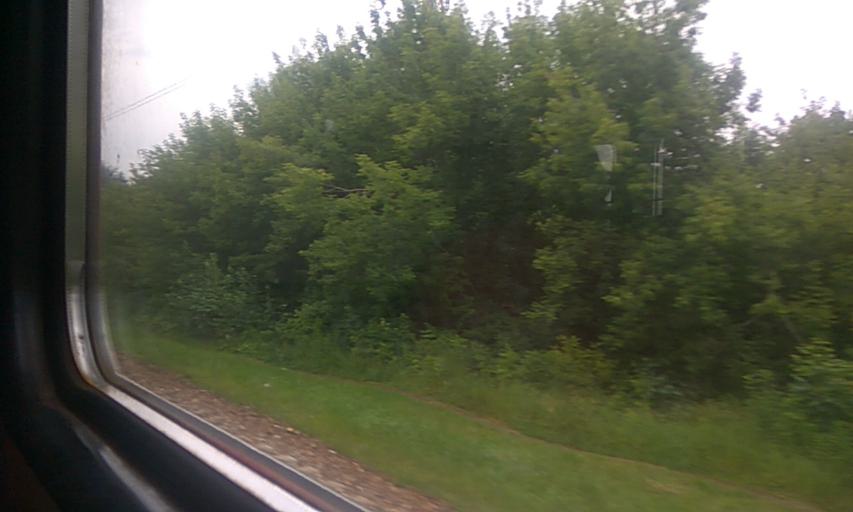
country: RU
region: Moskovskaya
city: Tomilino
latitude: 55.6528
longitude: 37.9669
